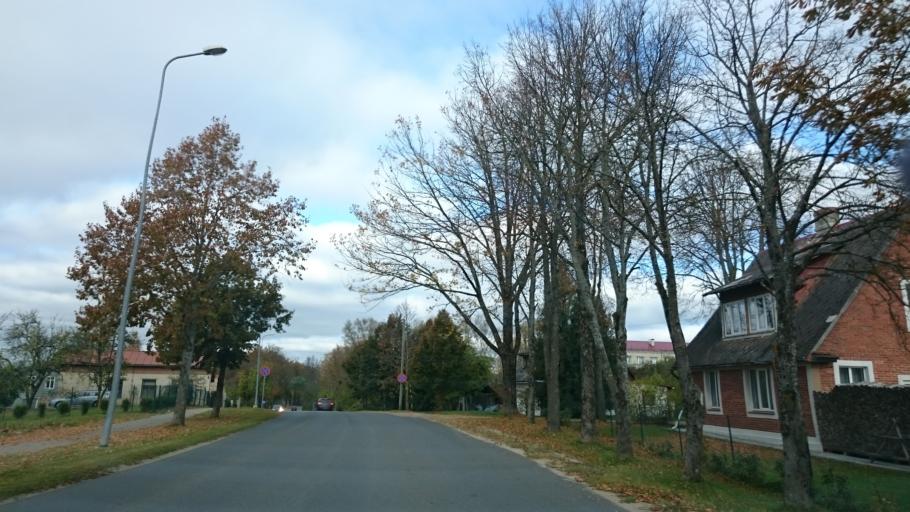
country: LV
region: Cesu Rajons
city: Cesis
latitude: 57.3026
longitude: 25.2688
